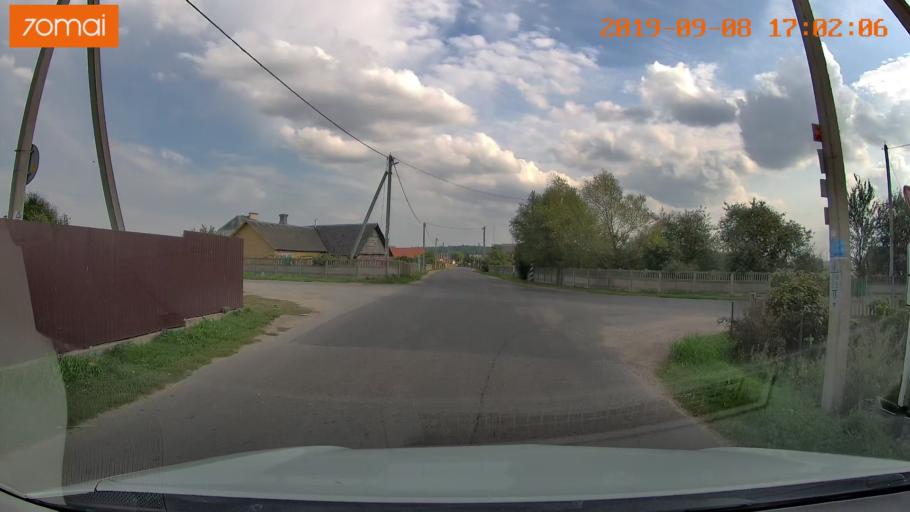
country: BY
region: Grodnenskaya
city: Hrodna
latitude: 53.7053
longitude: 23.9377
